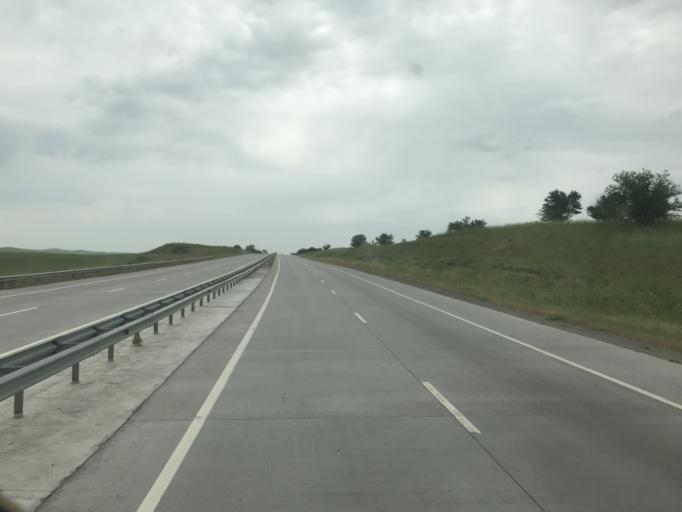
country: KZ
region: Ongtustik Qazaqstan
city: Shymkent
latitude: 42.2014
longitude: 69.5100
